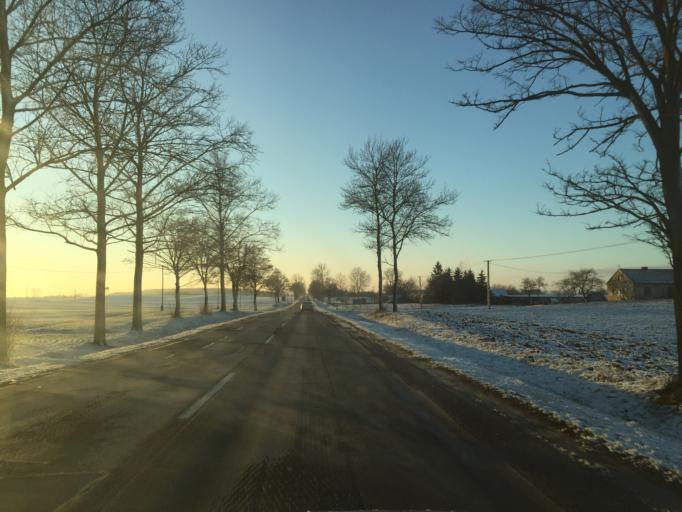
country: PL
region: Kujawsko-Pomorskie
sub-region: Powiat golubsko-dobrzynski
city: Golub-Dobrzyn
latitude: 53.1873
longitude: 19.0314
